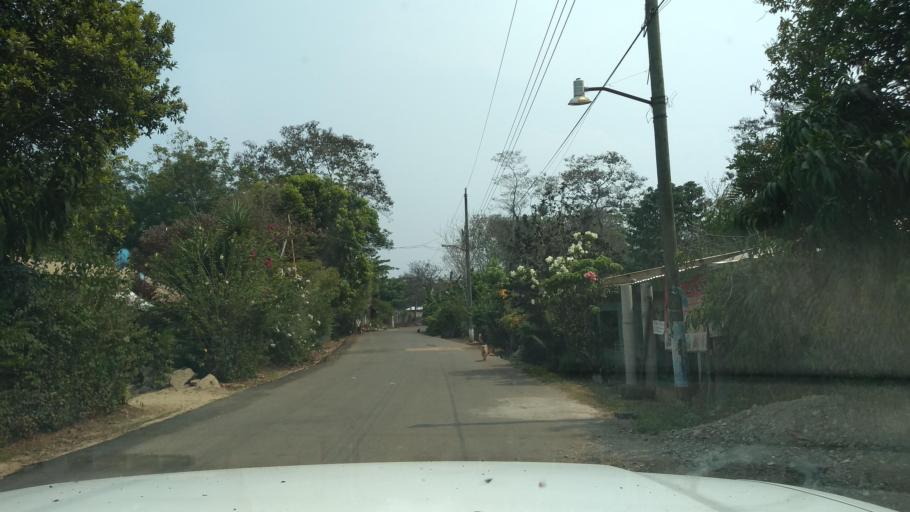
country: MX
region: Veracruz
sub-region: Tezonapa
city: Laguna Chica (Pueblo Nuevo)
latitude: 18.5417
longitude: -96.7809
